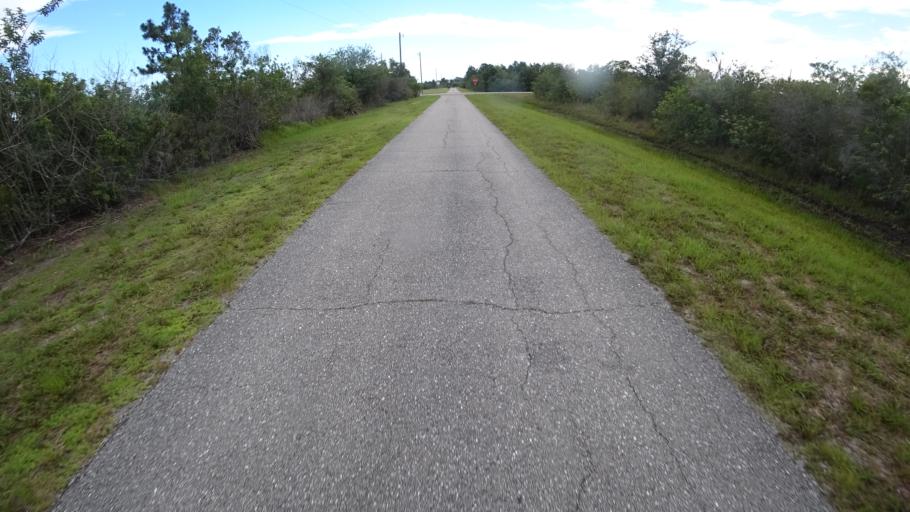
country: US
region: Florida
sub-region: Sarasota County
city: The Meadows
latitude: 27.4153
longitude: -82.2792
